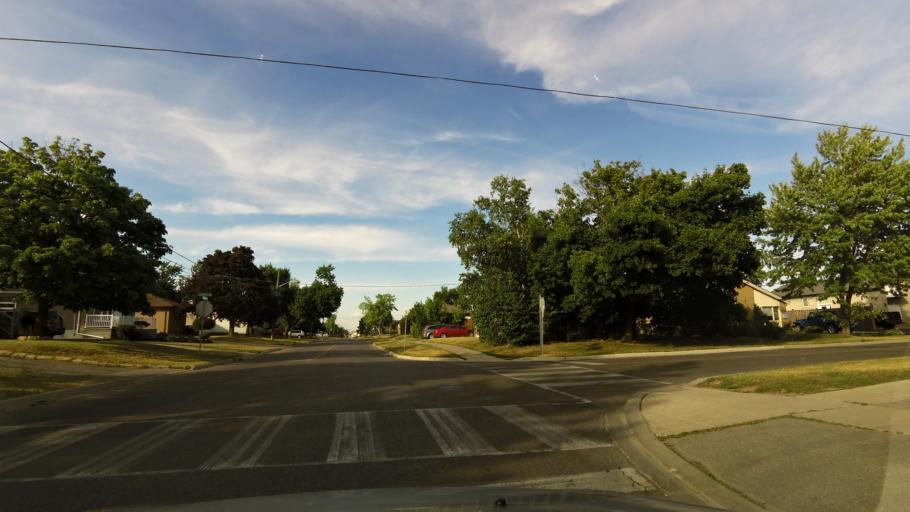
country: CA
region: Ontario
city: Brampton
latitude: 43.6833
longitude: -79.7428
